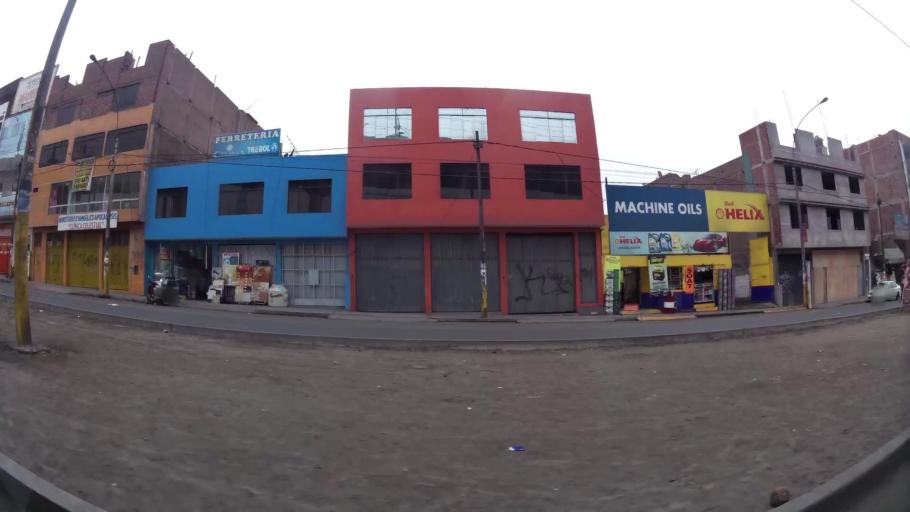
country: PE
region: Lima
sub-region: Lima
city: Independencia
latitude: -11.9623
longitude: -76.9892
